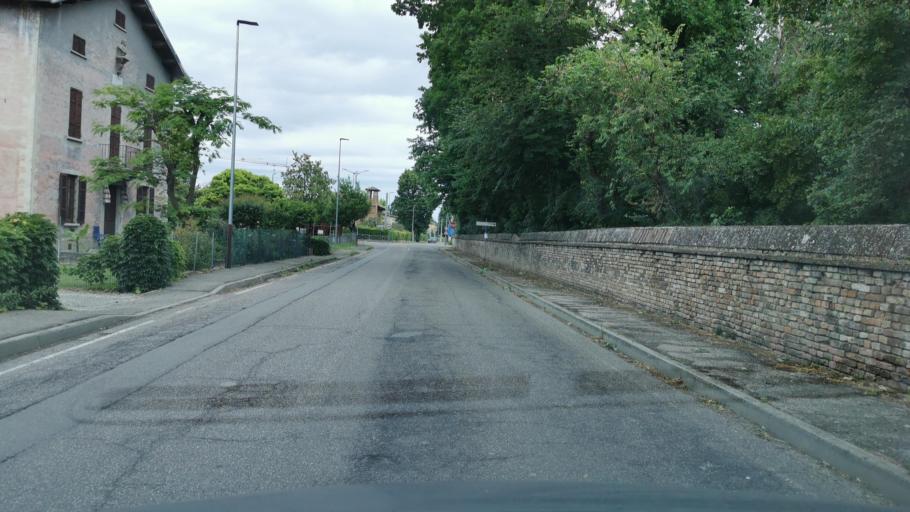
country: IT
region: Emilia-Romagna
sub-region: Provincia di Parma
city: Soragna
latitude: 44.9281
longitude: 10.1194
